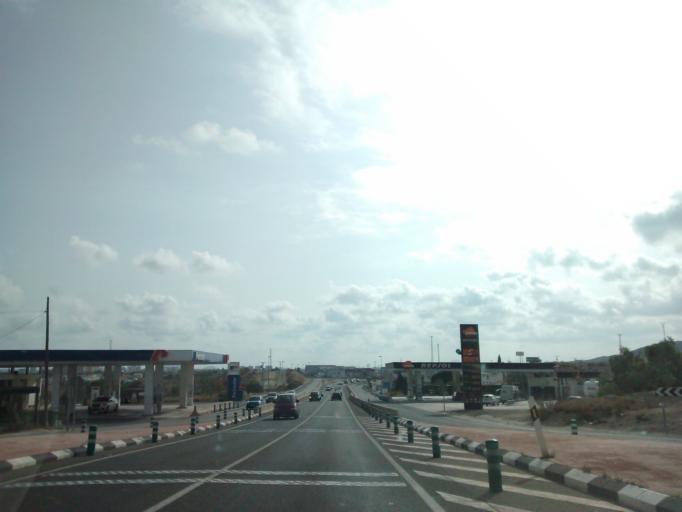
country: ES
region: Valencia
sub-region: Provincia de Alicante
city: el Campello
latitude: 38.4509
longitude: -0.3731
